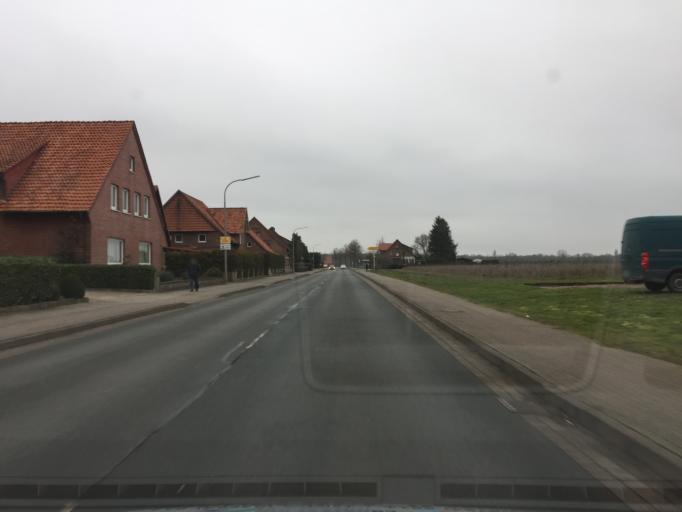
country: DE
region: Lower Saxony
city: Niedernwohren
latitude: 52.3563
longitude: 9.1416
